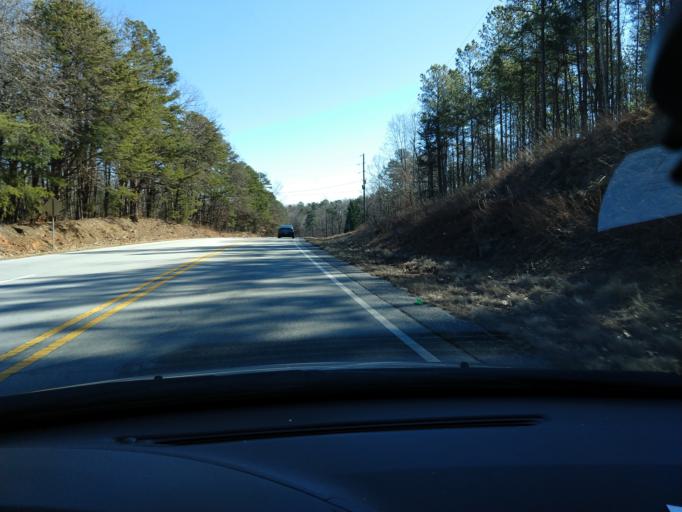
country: US
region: Georgia
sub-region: Stephens County
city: Toccoa
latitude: 34.6096
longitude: -83.3717
